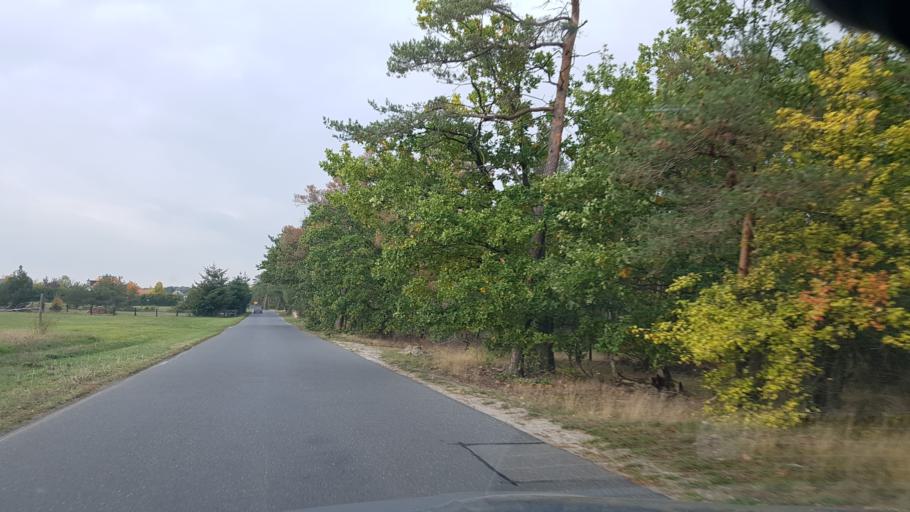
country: DE
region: Brandenburg
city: Elsterwerda
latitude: 51.4743
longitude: 13.4798
